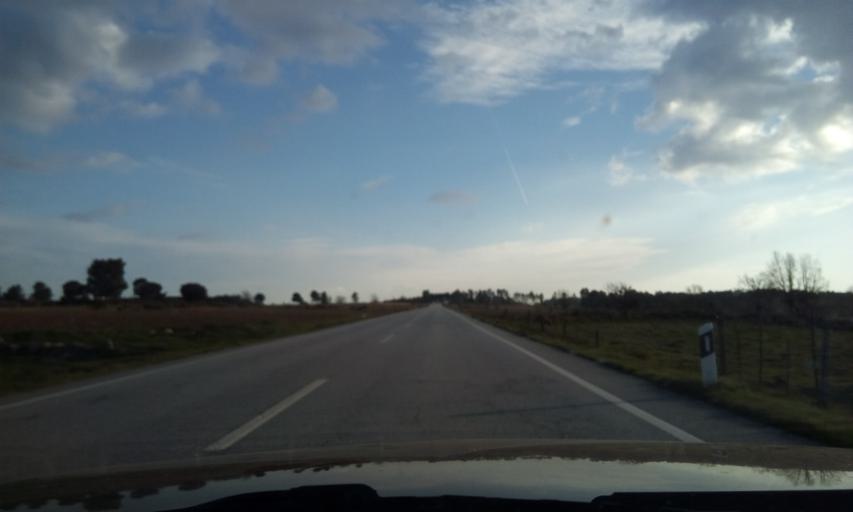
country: PT
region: Guarda
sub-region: Pinhel
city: Pinhel
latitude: 40.6502
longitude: -6.9674
